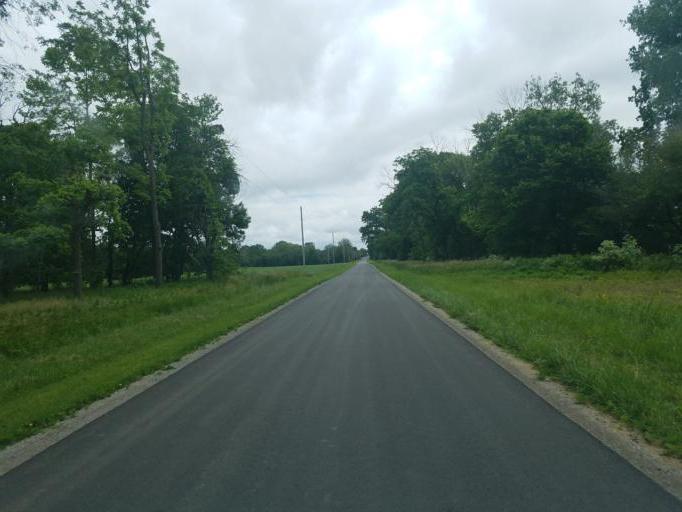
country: US
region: Ohio
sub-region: Wyandot County
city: Upper Sandusky
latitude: 40.7748
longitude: -83.1792
